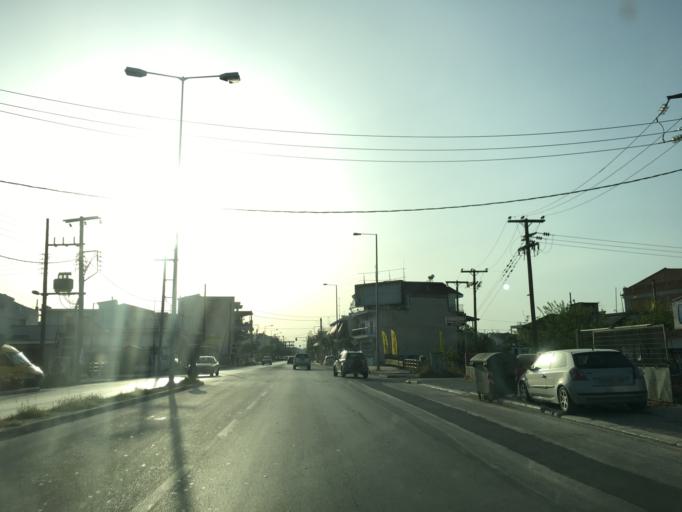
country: GR
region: Thessaly
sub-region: Nomos Larisis
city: Larisa
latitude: 39.6315
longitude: 22.4461
